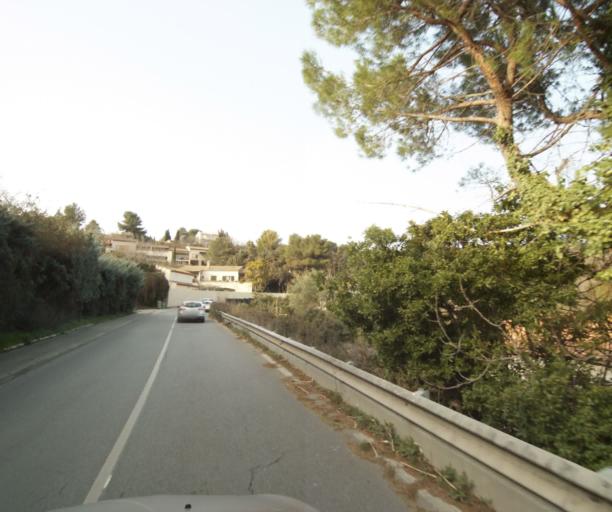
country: FR
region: Provence-Alpes-Cote d'Azur
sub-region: Departement des Bouches-du-Rhone
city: Eguilles
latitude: 43.5672
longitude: 5.3597
